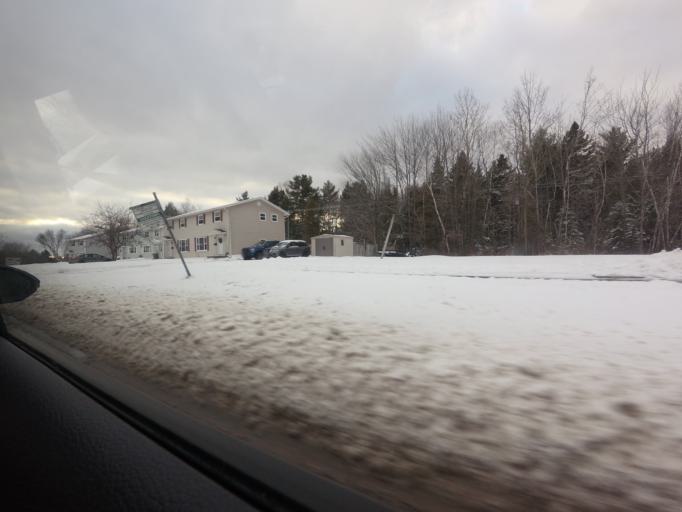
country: CA
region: New Brunswick
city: Oromocto
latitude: 45.8439
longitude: -66.4901
